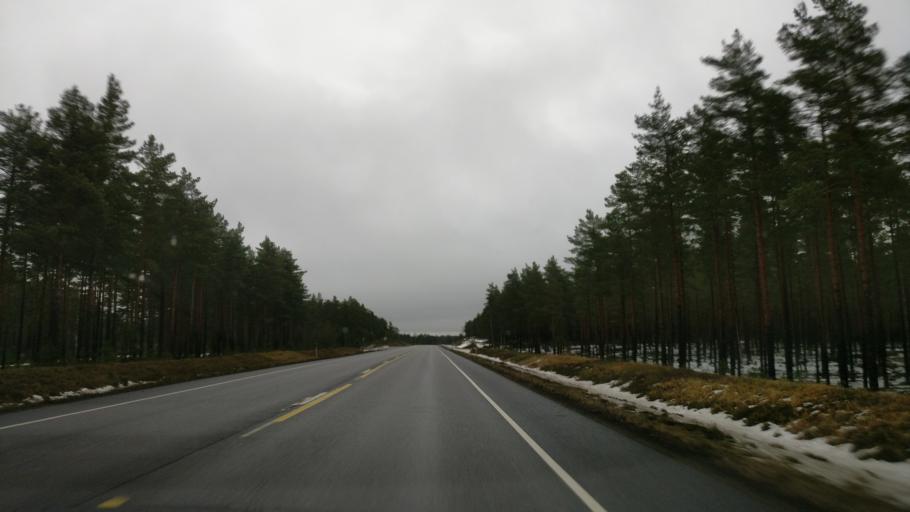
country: FI
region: Uusimaa
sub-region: Raaseporin
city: Hanko
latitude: 59.8941
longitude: 23.1824
